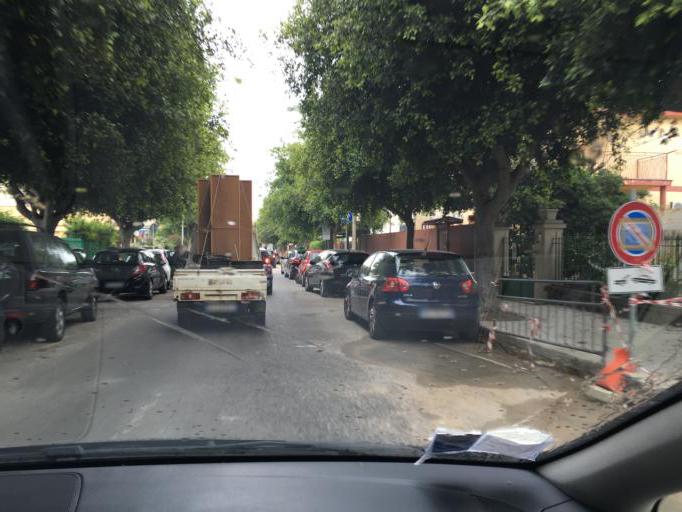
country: IT
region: Sicily
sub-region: Palermo
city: Palermo
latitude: 38.1965
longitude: 13.3151
